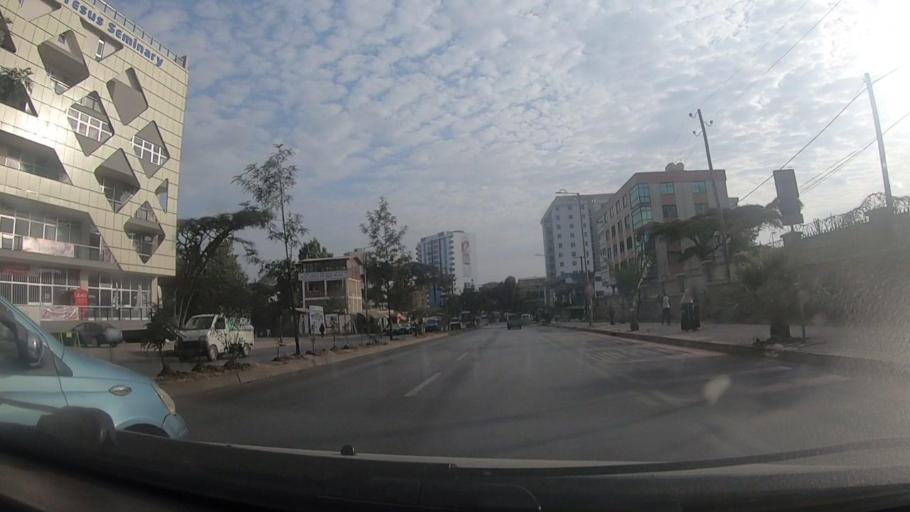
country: ET
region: Adis Abeba
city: Addis Ababa
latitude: 8.9700
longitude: 38.7313
